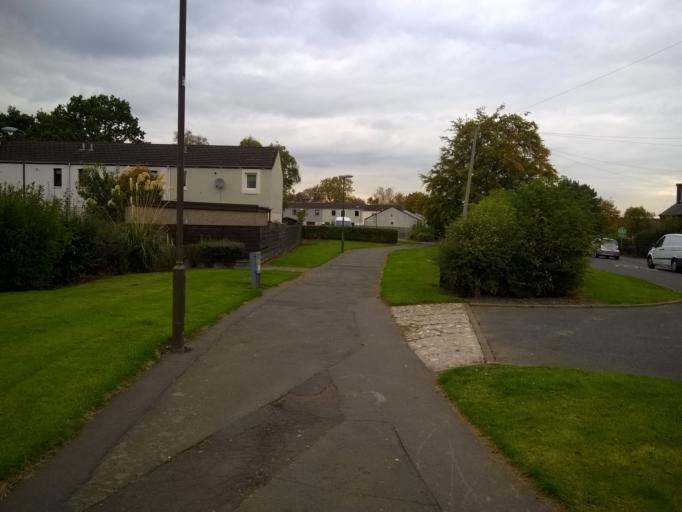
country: GB
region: Scotland
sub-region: West Lothian
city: Mid Calder
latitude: 55.8790
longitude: -3.4977
